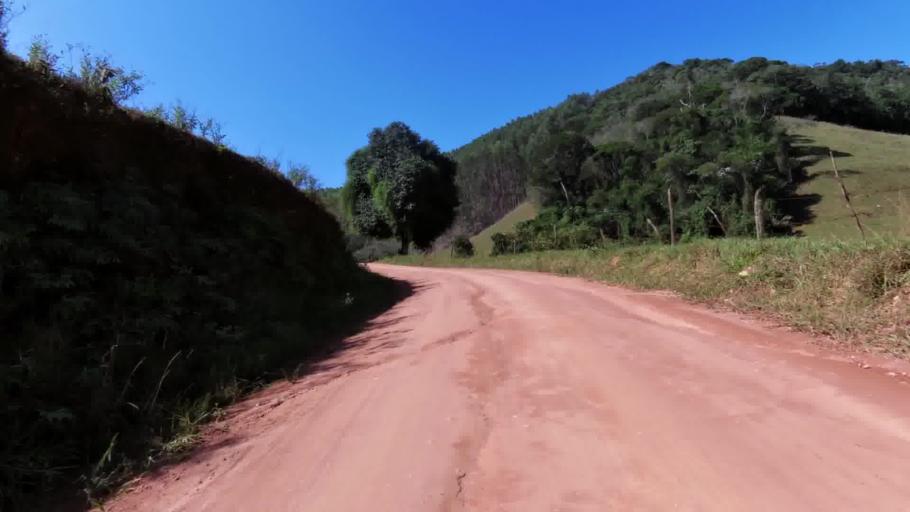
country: BR
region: Espirito Santo
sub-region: Alfredo Chaves
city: Alfredo Chaves
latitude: -20.5678
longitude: -40.7782
